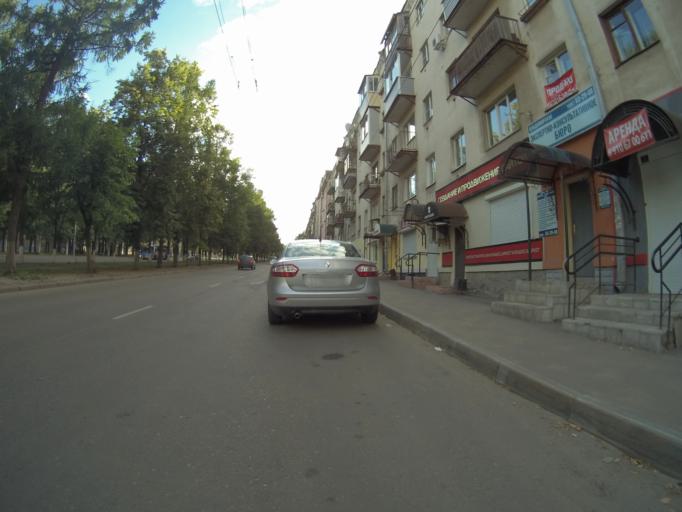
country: RU
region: Vladimir
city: Vladimir
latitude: 56.1444
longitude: 40.4158
